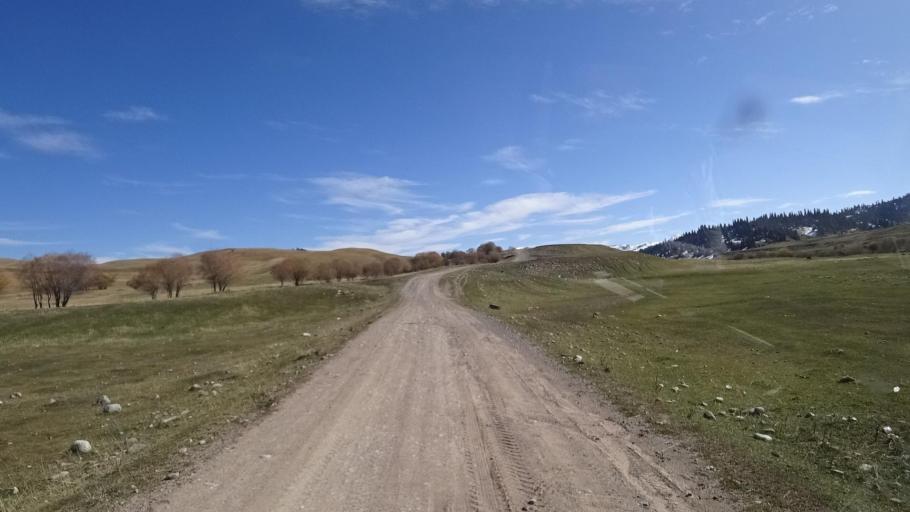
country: KZ
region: Almaty Oblysy
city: Kegen
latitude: 42.7373
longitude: 79.0128
